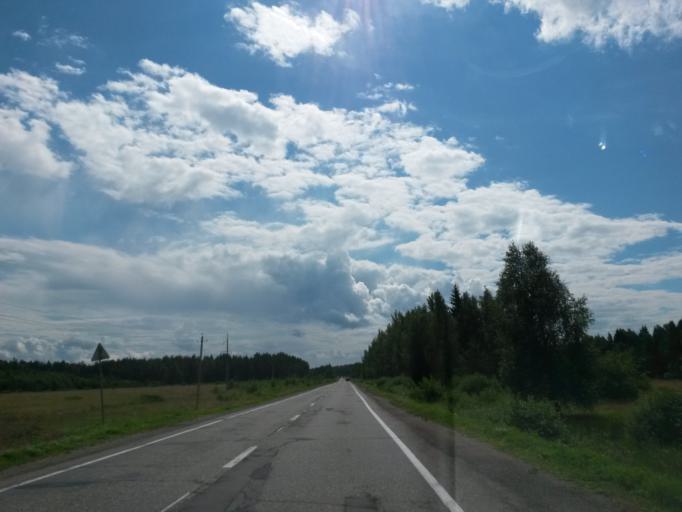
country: RU
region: Jaroslavl
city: Gavrilov-Yam
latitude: 57.3011
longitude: 39.9483
